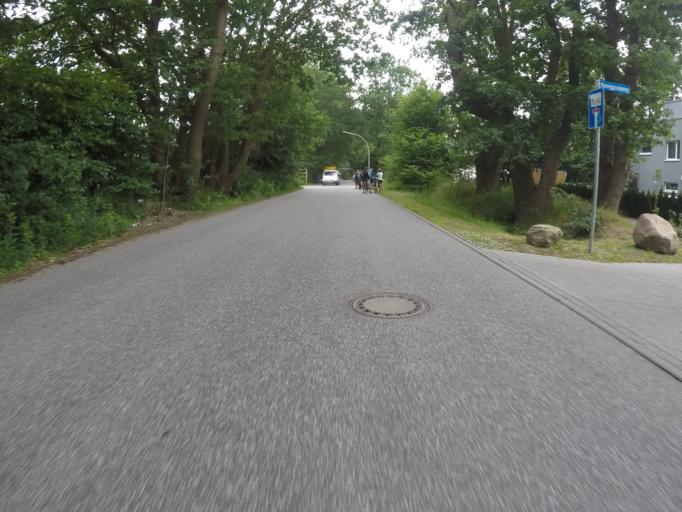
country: DE
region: Hamburg
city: Wandsbek
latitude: 53.5645
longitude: 10.1332
